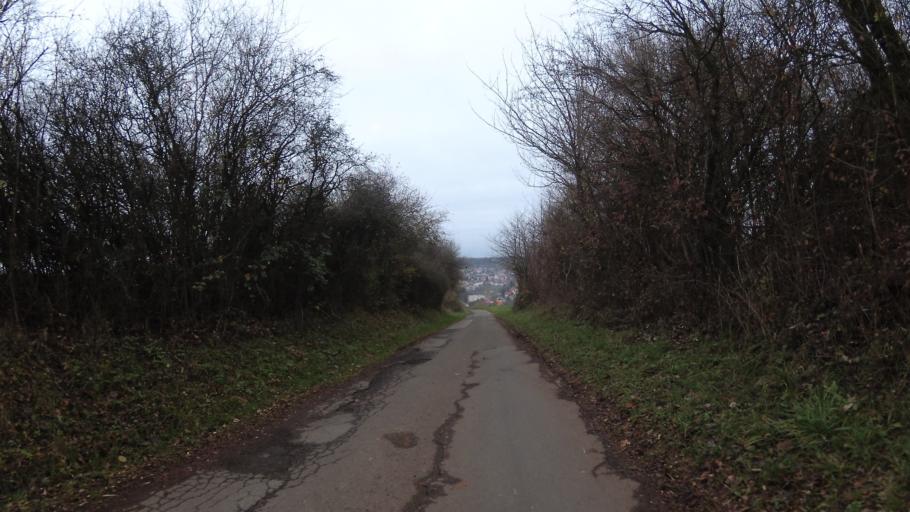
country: DE
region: Saarland
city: Mainzweiler
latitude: 49.4248
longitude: 7.0887
